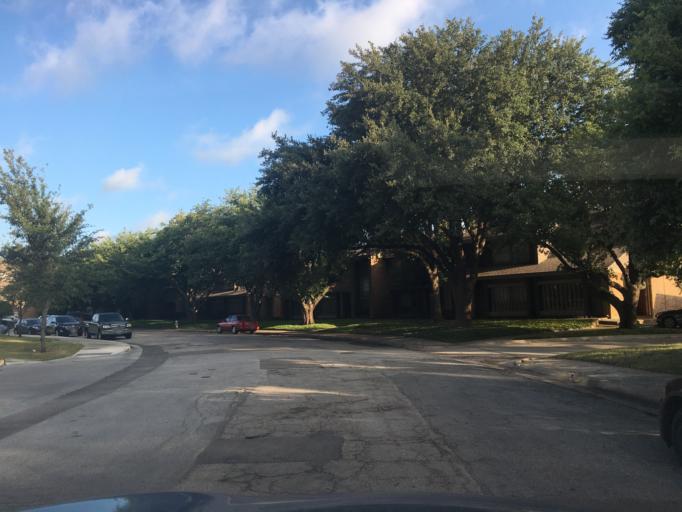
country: US
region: Texas
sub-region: Dallas County
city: Highland Park
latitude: 32.8493
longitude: -96.7623
